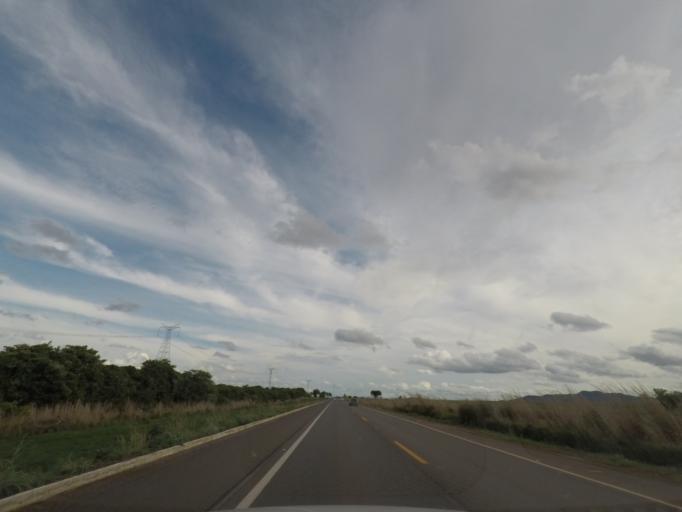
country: BR
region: Goias
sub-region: Padre Bernardo
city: Padre Bernardo
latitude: -15.4542
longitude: -48.6150
